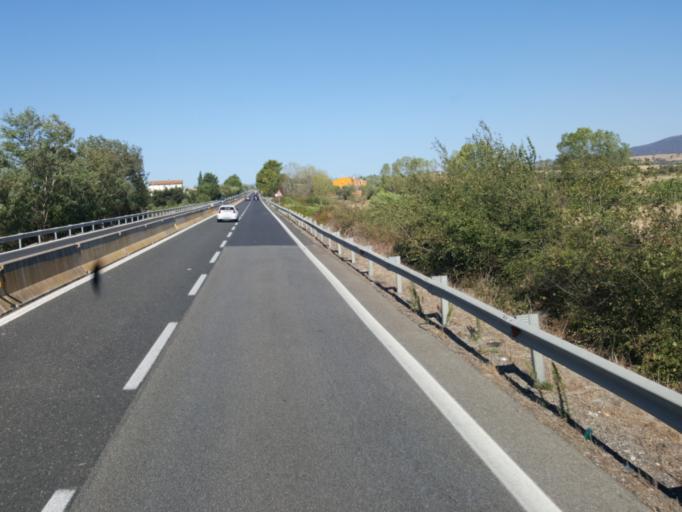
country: IT
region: Latium
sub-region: Provincia di Viterbo
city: Pescia Romana
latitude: 42.4037
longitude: 11.4952
